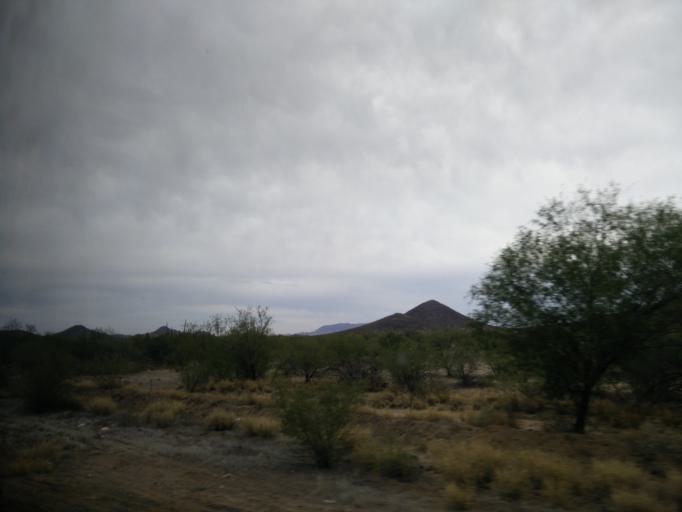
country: MX
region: Sonora
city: Hermosillo
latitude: 28.8219
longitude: -110.9580
